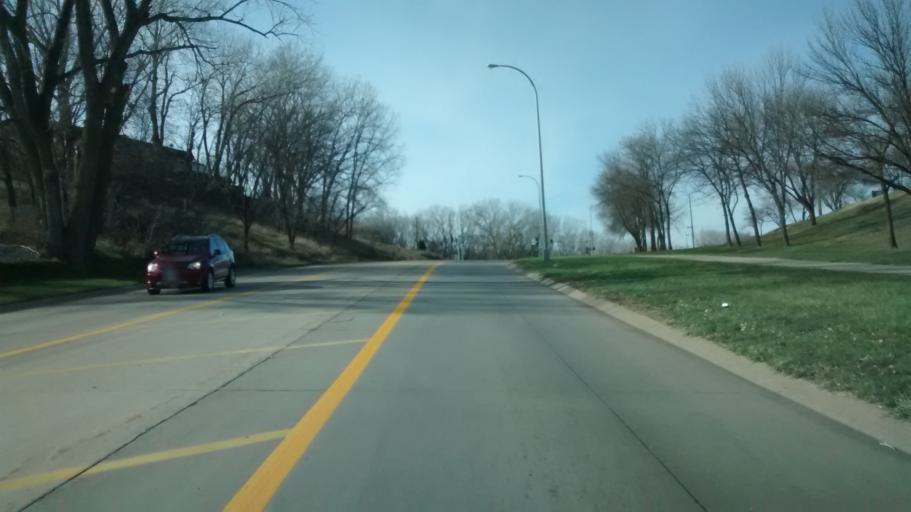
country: US
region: Iowa
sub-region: Woodbury County
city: Sioux City
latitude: 42.5409
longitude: -96.3915
